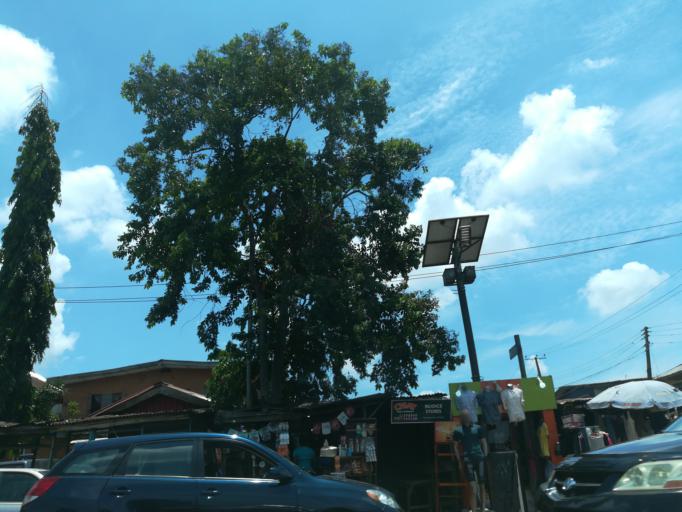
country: NG
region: Lagos
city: Ikorodu
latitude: 6.6120
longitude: 3.5006
